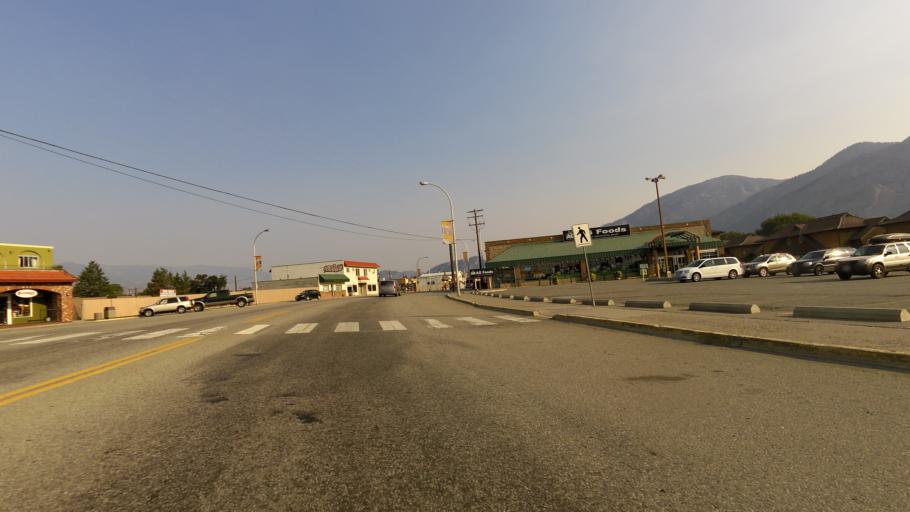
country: CA
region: British Columbia
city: Osoyoos
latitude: 49.0303
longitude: -119.4628
